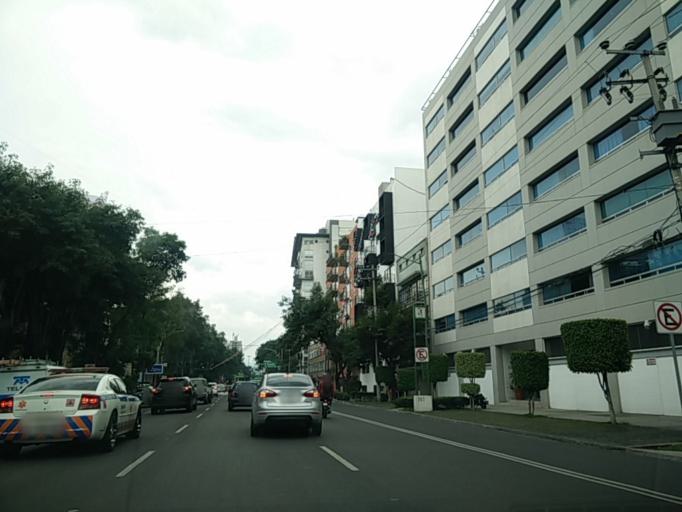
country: MX
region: Mexico City
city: Colonia del Valle
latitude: 19.3842
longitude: -99.1577
